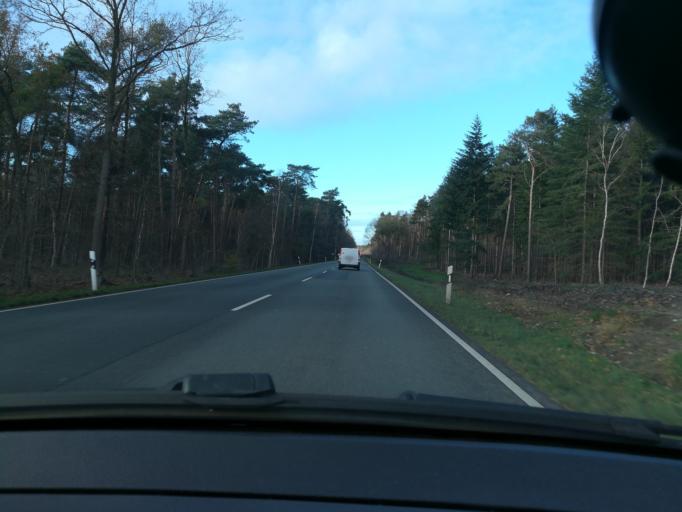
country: DE
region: Lower Saxony
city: Uchte
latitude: 52.5339
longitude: 8.8772
